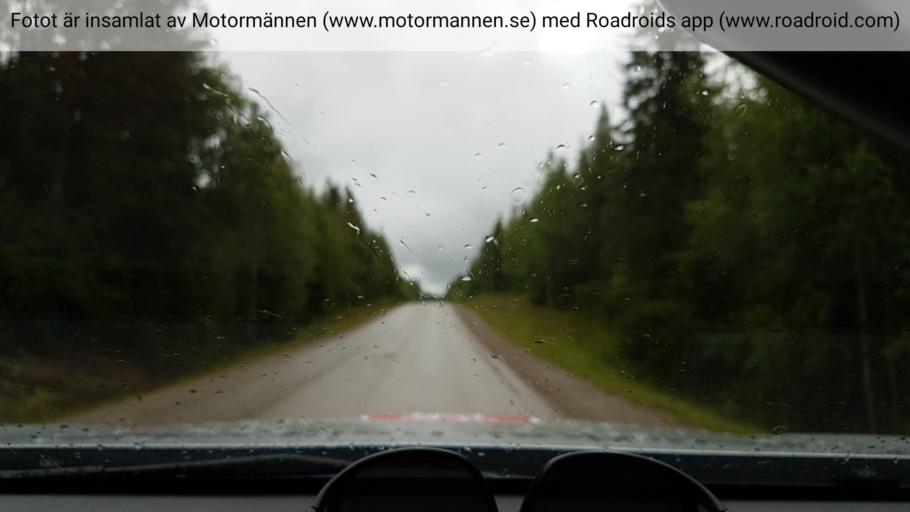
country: SE
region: Vaesterbotten
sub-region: Asele Kommun
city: Insjon
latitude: 64.8005
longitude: 17.6052
